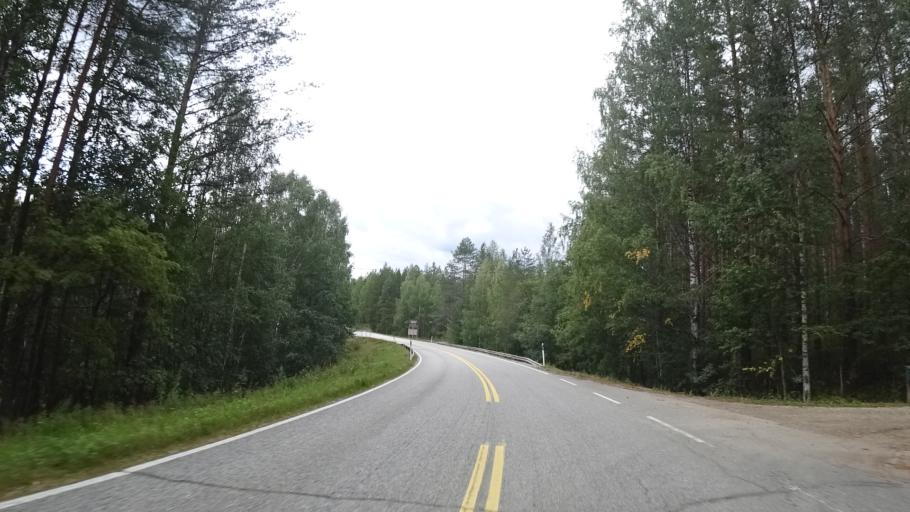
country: FI
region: North Karelia
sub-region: Joensuu
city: Ilomantsi
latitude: 62.6229
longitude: 31.1949
